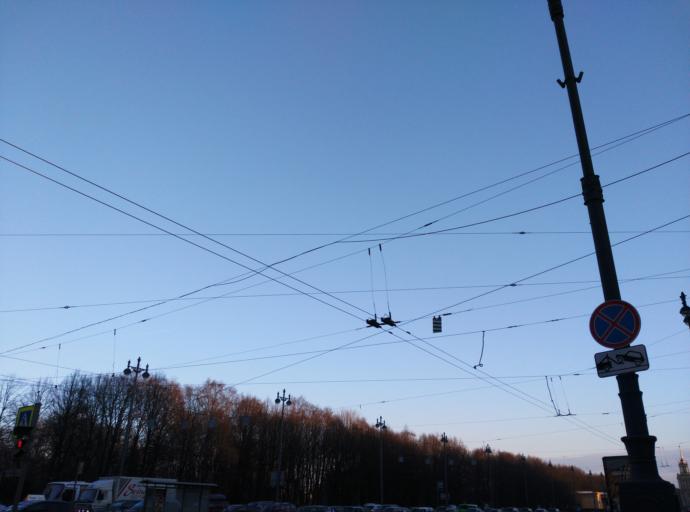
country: RU
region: St.-Petersburg
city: Kupchino
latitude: 59.8716
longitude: 30.3199
